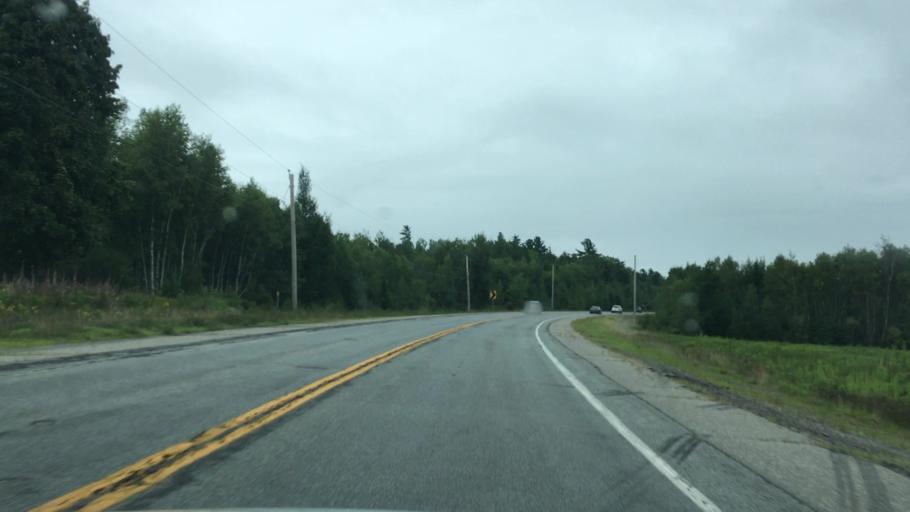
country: US
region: Maine
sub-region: Washington County
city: Cherryfield
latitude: 44.8554
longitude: -68.0554
